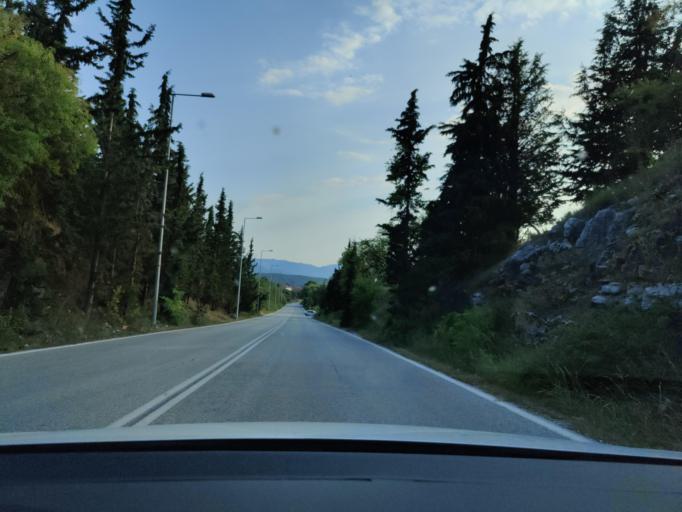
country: GR
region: East Macedonia and Thrace
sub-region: Nomos Kavalas
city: Zygos
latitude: 40.9922
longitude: 24.3785
